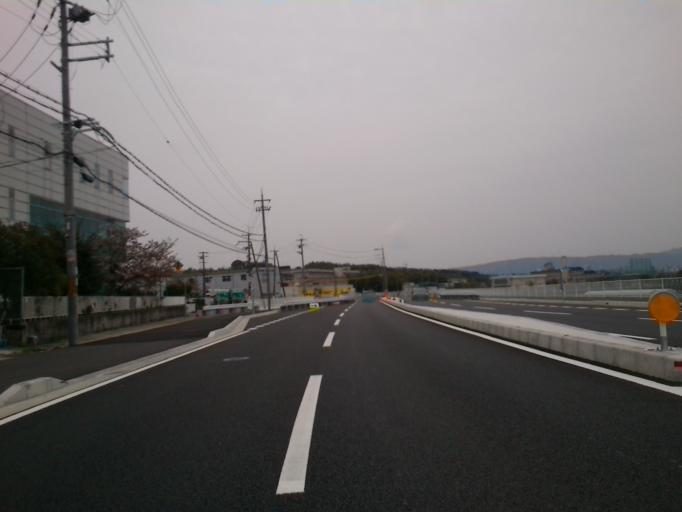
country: JP
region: Kyoto
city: Yawata
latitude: 34.8505
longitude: 135.7258
